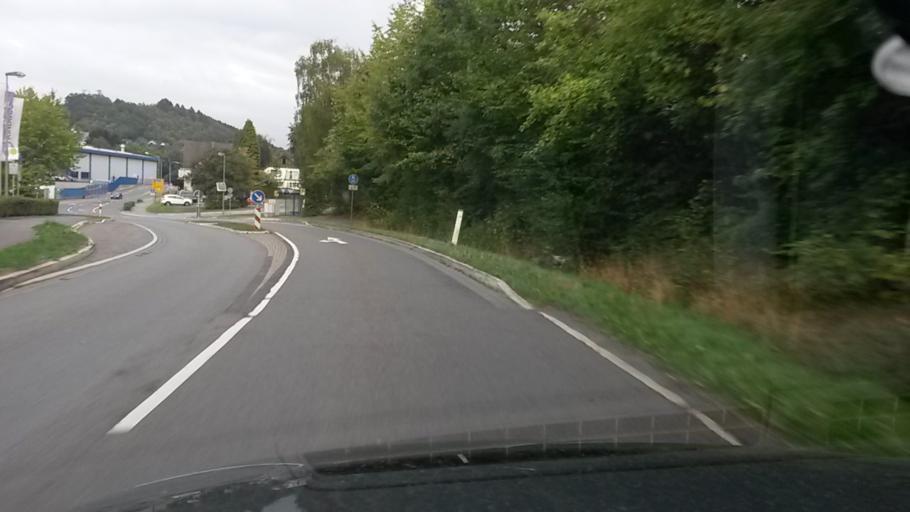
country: DE
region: North Rhine-Westphalia
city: Wiehl
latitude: 50.9639
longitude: 7.4919
